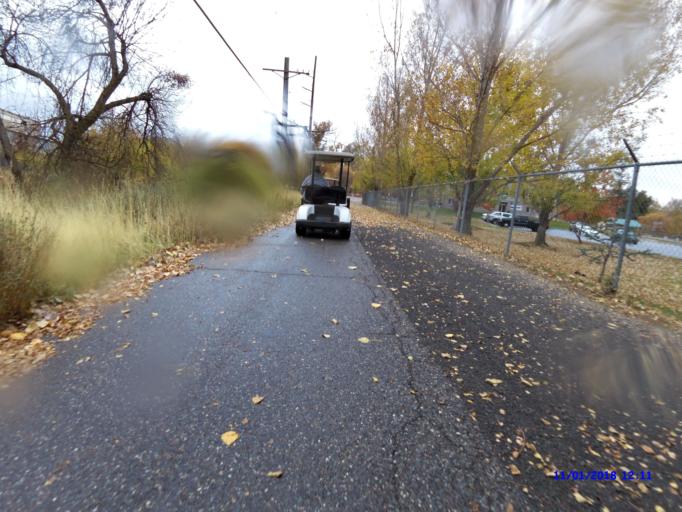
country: US
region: Utah
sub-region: Weber County
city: Ogden
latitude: 41.2245
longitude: -111.9882
